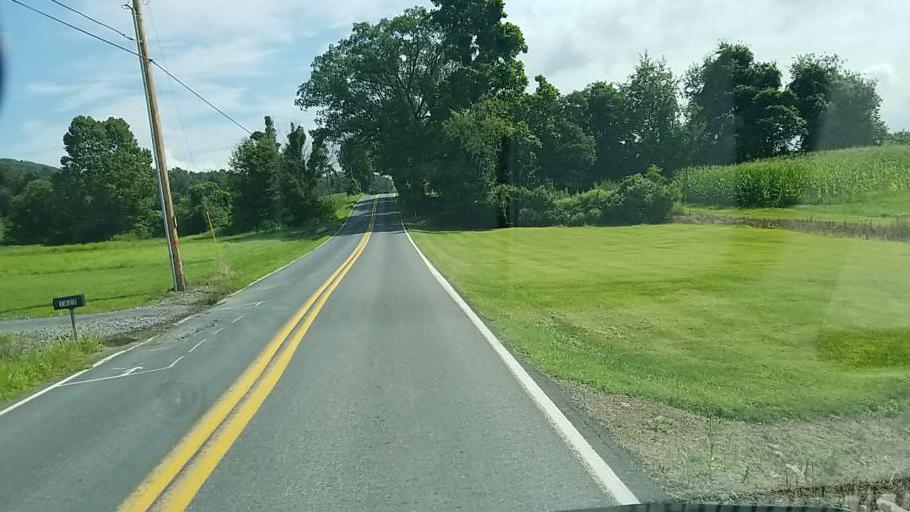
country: US
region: Pennsylvania
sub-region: Dauphin County
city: Millersburg
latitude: 40.5807
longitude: -76.9314
